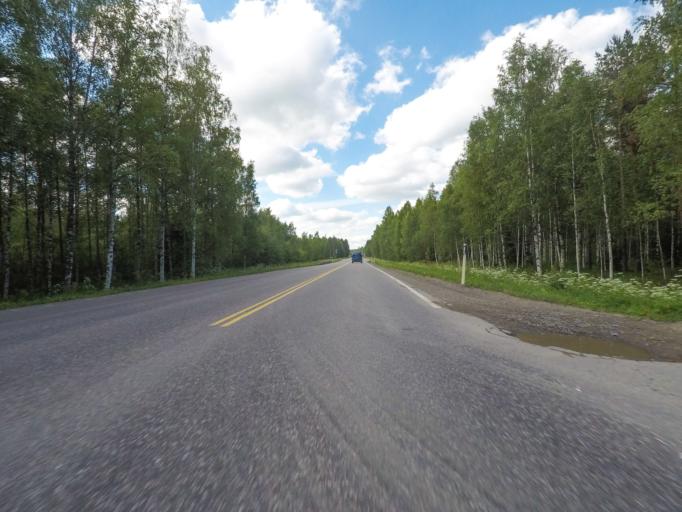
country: FI
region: Southern Savonia
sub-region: Savonlinna
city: Kerimaeki
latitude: 61.8342
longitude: 29.2255
